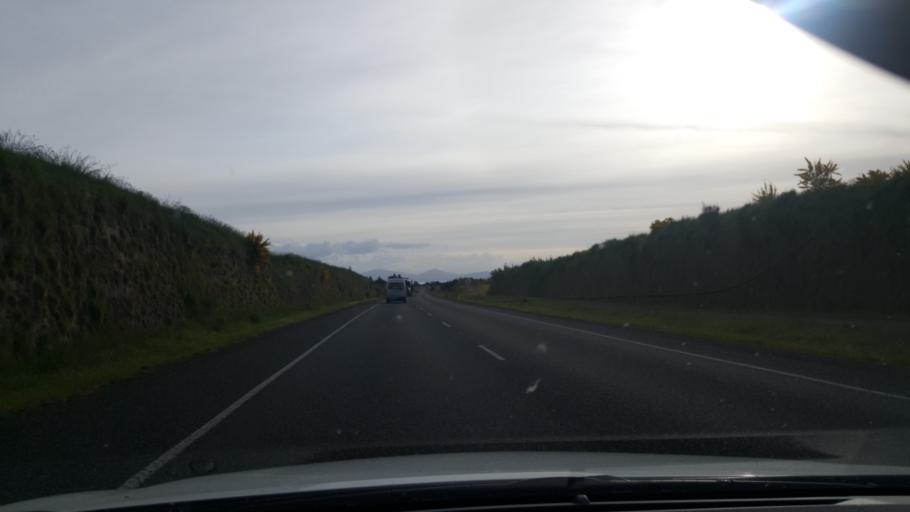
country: NZ
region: Waikato
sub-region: Taupo District
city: Taupo
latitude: -38.7242
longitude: 176.0963
